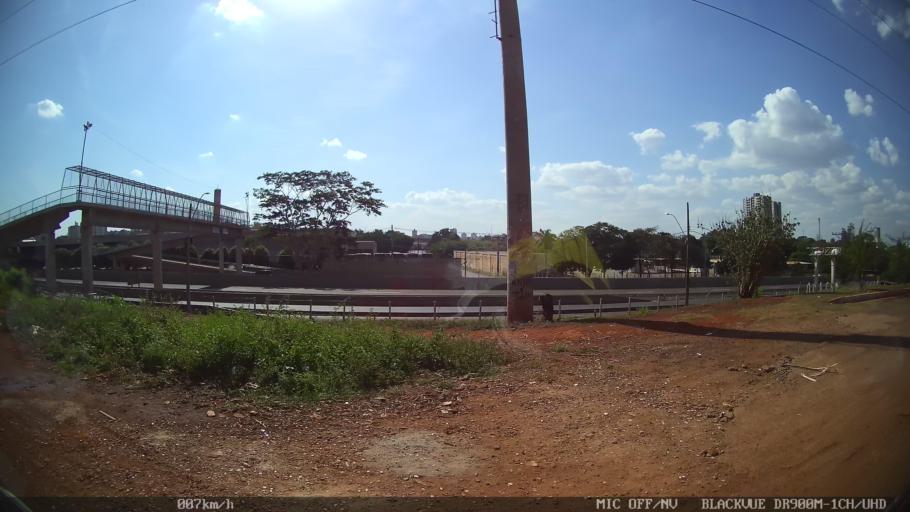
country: BR
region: Sao Paulo
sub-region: Ribeirao Preto
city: Ribeirao Preto
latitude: -21.1788
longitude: -47.8334
